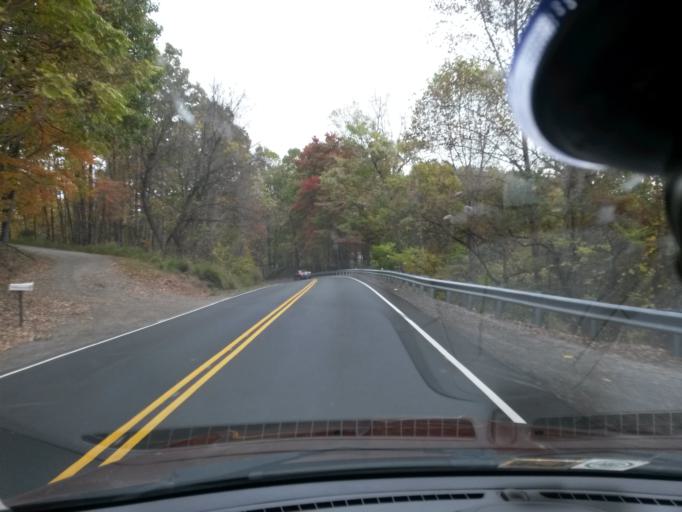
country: US
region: Virginia
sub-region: Roanoke County
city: Narrows
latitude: 37.2039
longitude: -79.8813
